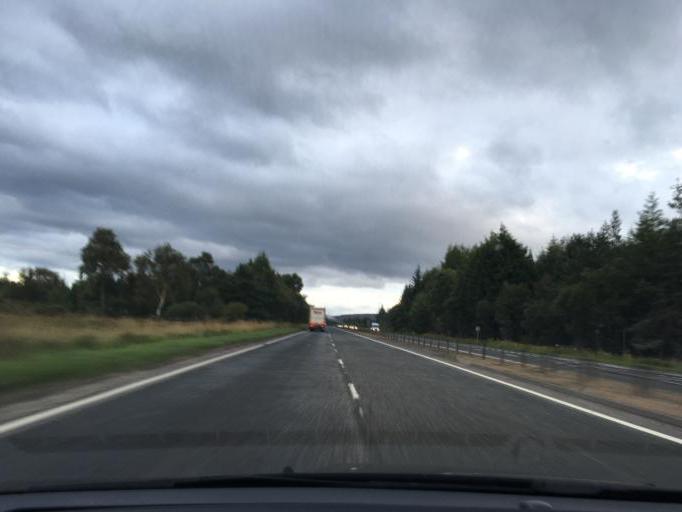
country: GB
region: Scotland
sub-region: Highland
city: Inverness
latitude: 57.4458
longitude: -4.1510
